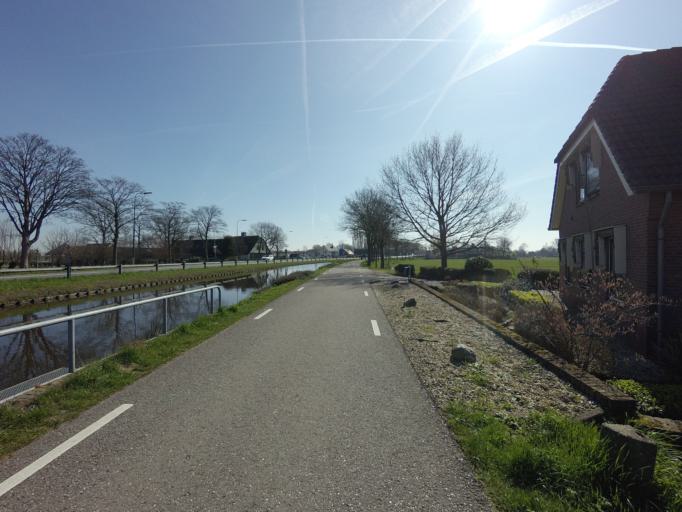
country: NL
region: Utrecht
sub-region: Gemeente Woerden
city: Woerden
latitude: 52.0668
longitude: 4.9063
